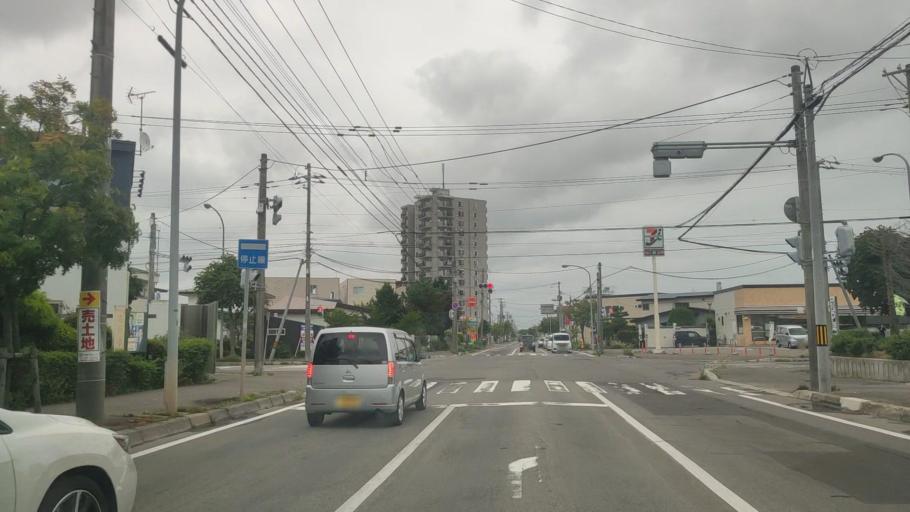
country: JP
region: Hokkaido
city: Hakodate
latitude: 41.7987
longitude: 140.7618
